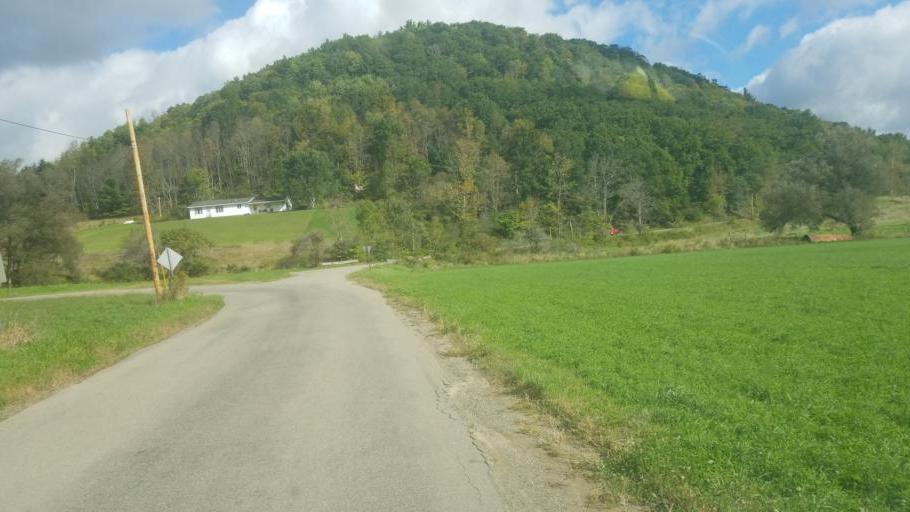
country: US
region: New York
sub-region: Cattaraugus County
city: Weston Mills
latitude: 42.1358
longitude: -78.3442
